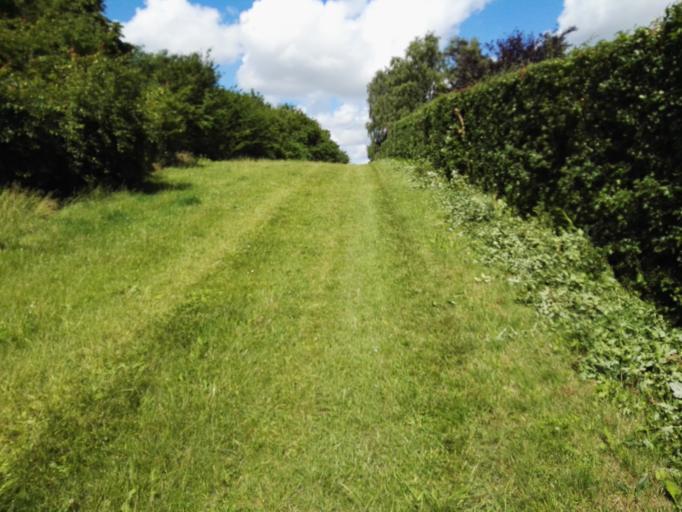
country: DK
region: Capital Region
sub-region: Ballerup Kommune
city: Ballerup
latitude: 55.7357
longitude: 12.3747
